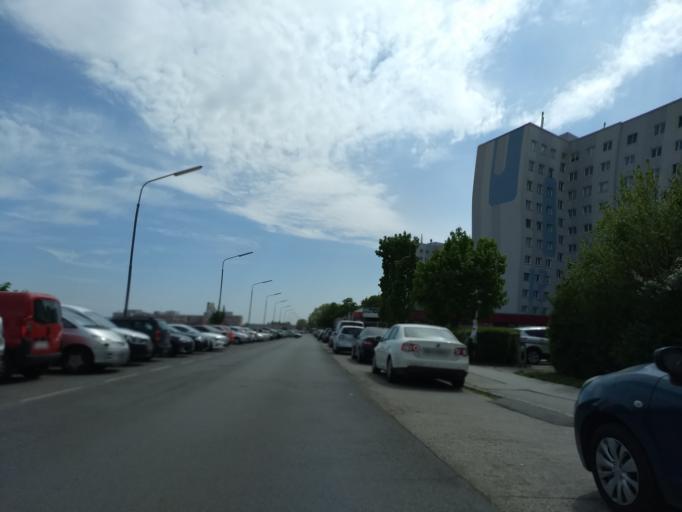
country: AT
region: Lower Austria
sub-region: Politischer Bezirk Wien-Umgebung
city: Gerasdorf bei Wien
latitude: 48.2425
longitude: 16.4819
